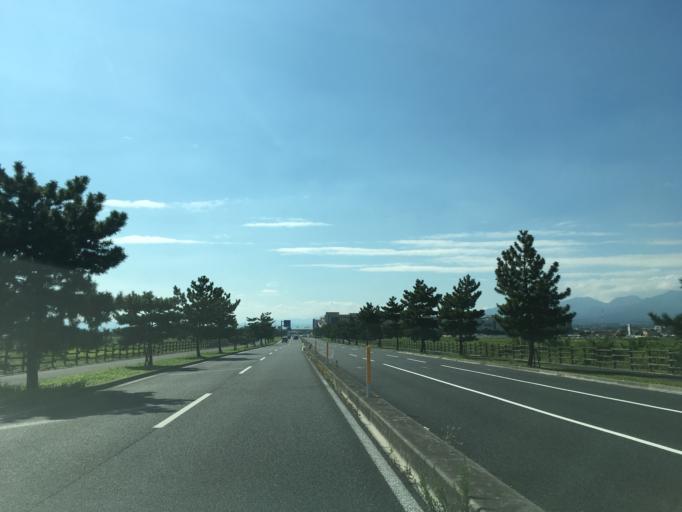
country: JP
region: Gunma
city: Kanekomachi
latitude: 36.3888
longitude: 139.0151
